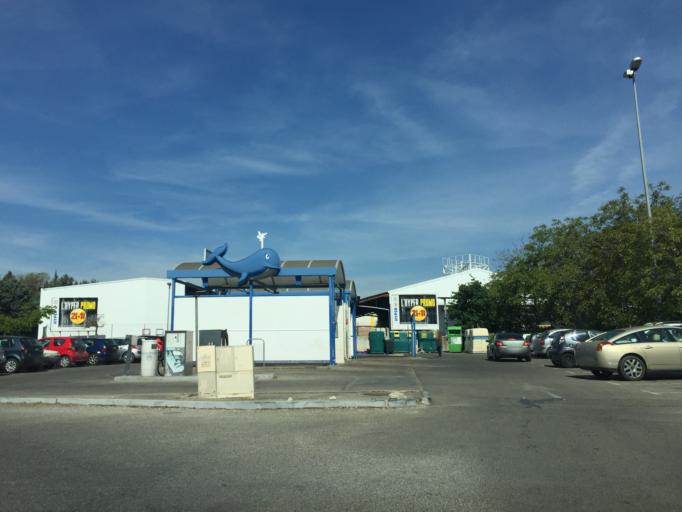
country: FR
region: Provence-Alpes-Cote d'Azur
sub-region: Departement des Alpes-de-Haute-Provence
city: Manosque
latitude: 43.8193
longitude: 5.7983
